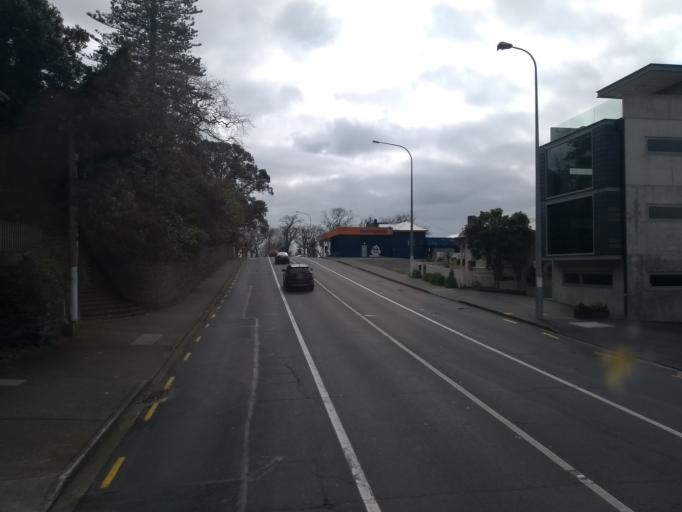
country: NZ
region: Auckland
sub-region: Auckland
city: Auckland
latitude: -36.8653
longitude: 174.7707
